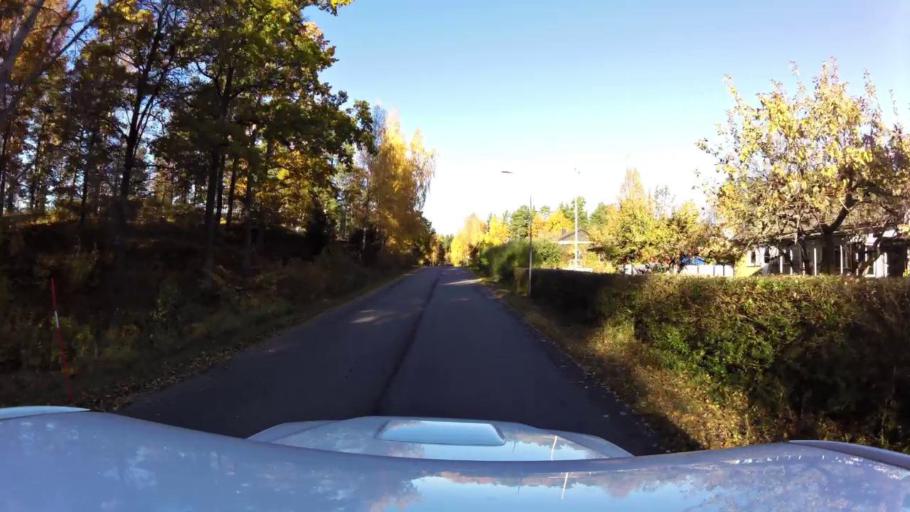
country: SE
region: OEstergoetland
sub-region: Linkopings Kommun
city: Ljungsbro
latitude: 58.5183
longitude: 15.4954
